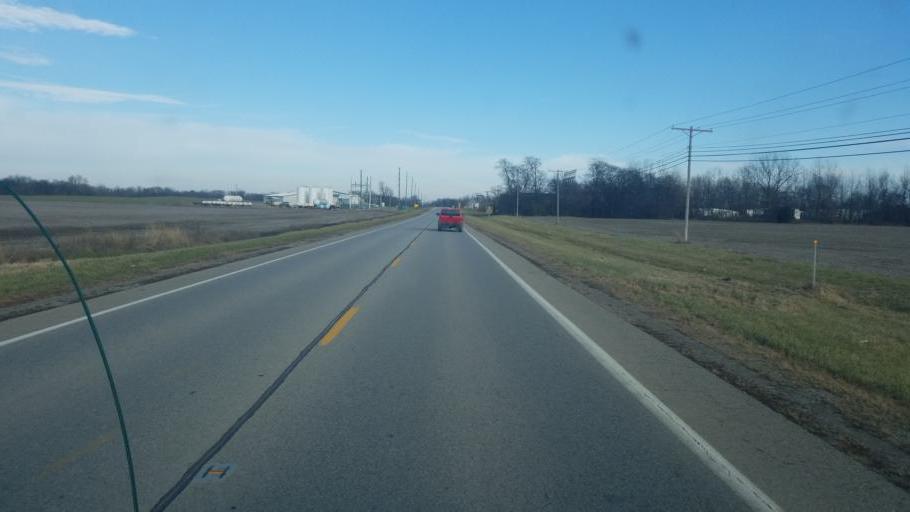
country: US
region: Illinois
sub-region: White County
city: Carmi
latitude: 38.1035
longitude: -88.1367
